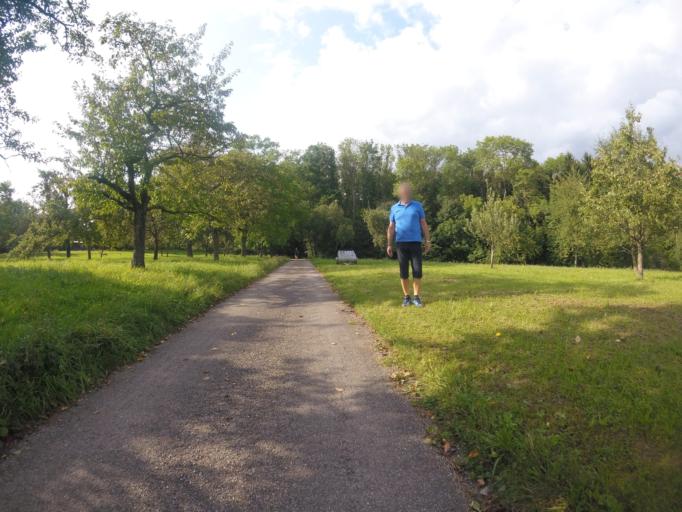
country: DE
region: Baden-Wuerttemberg
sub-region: Regierungsbezirk Stuttgart
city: Aspach
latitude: 48.9973
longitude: 9.4170
